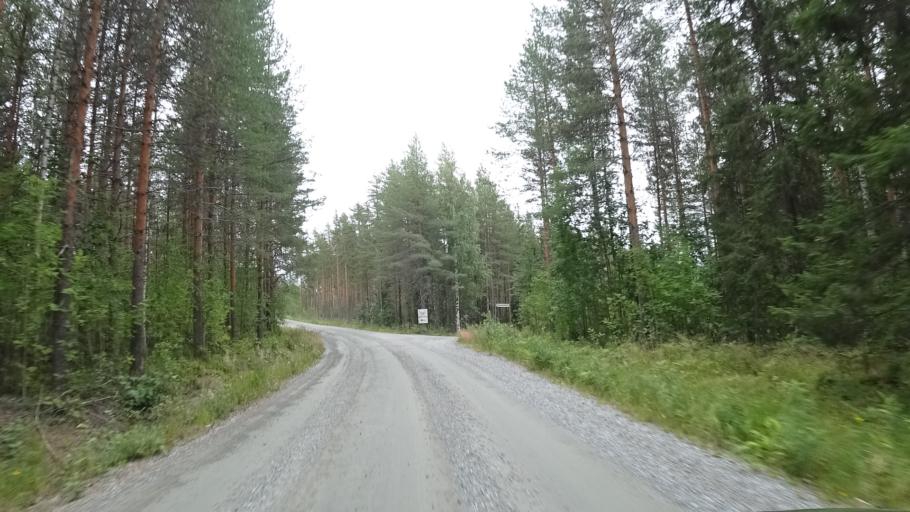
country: FI
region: North Karelia
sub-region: Pielisen Karjala
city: Lieksa
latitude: 63.3742
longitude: 30.3656
